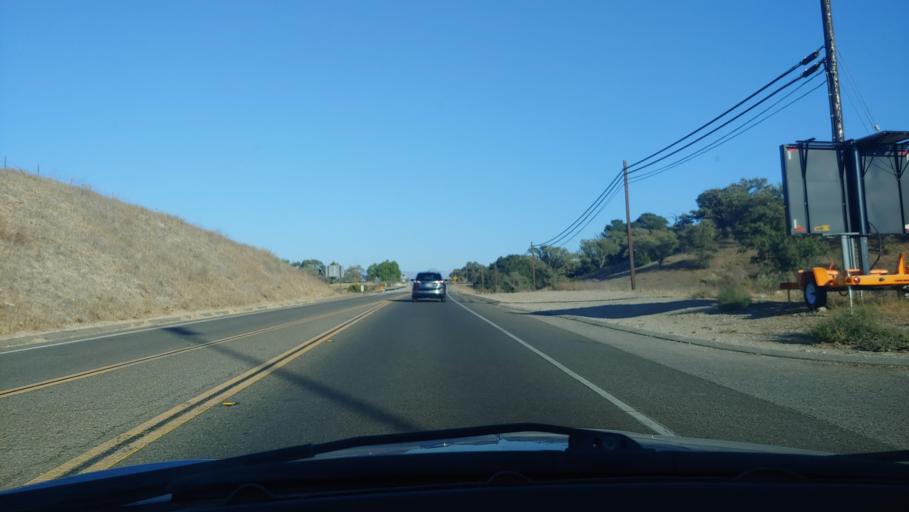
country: US
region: California
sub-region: Santa Barbara County
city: Santa Ynez
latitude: 34.6104
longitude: -120.0809
